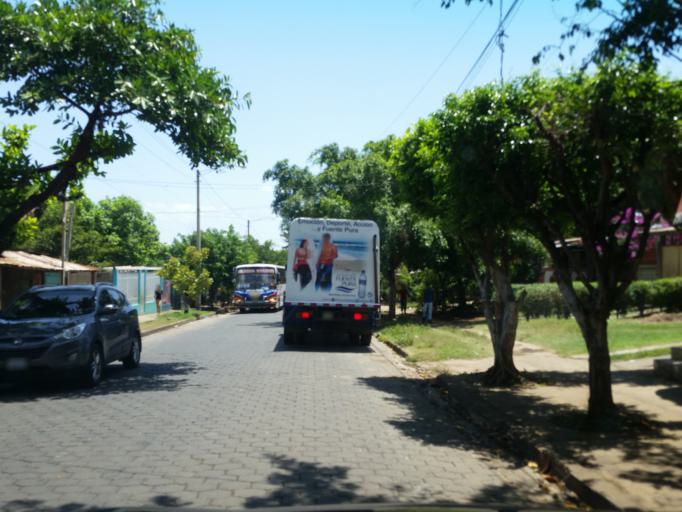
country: NI
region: Managua
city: Managua
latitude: 12.1124
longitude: -86.2338
